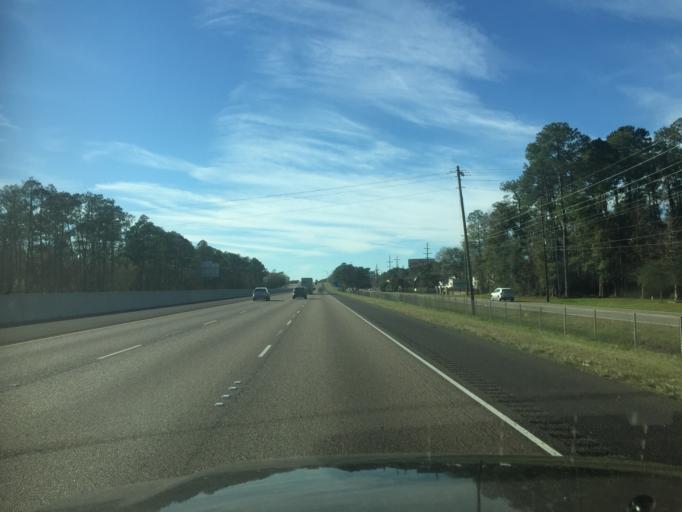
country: US
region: Louisiana
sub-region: Saint Tammany Parish
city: Slidell
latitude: 30.3103
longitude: -89.7612
